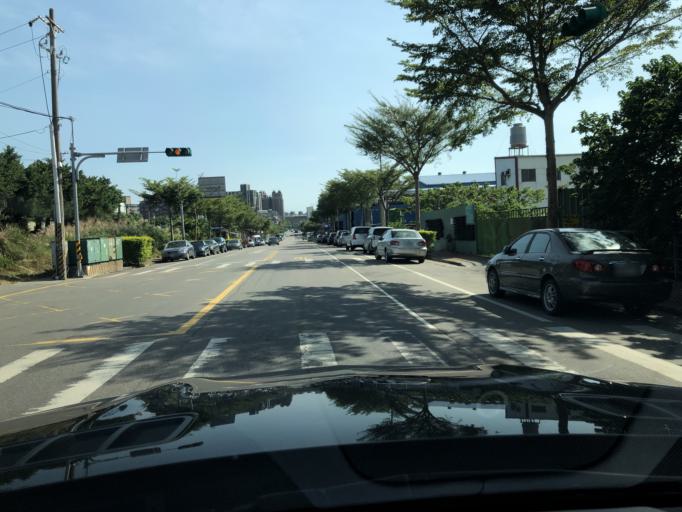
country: TW
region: Taiwan
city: Taoyuan City
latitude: 25.0656
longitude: 121.2910
